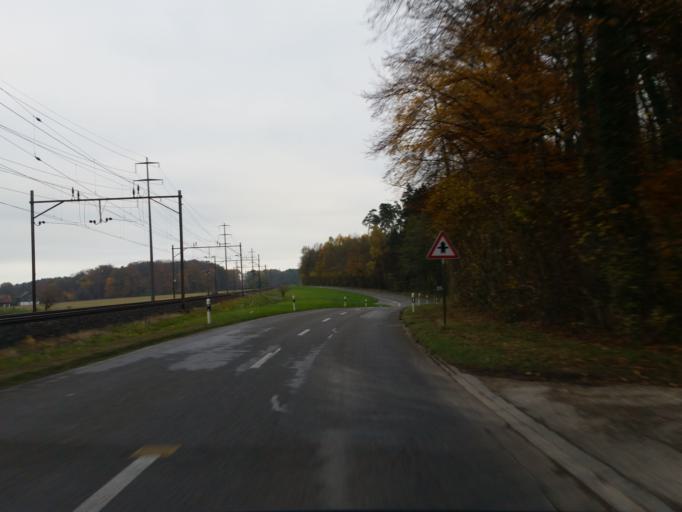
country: CH
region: Thurgau
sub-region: Arbon District
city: Amriswil
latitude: 47.5488
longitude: 9.3197
